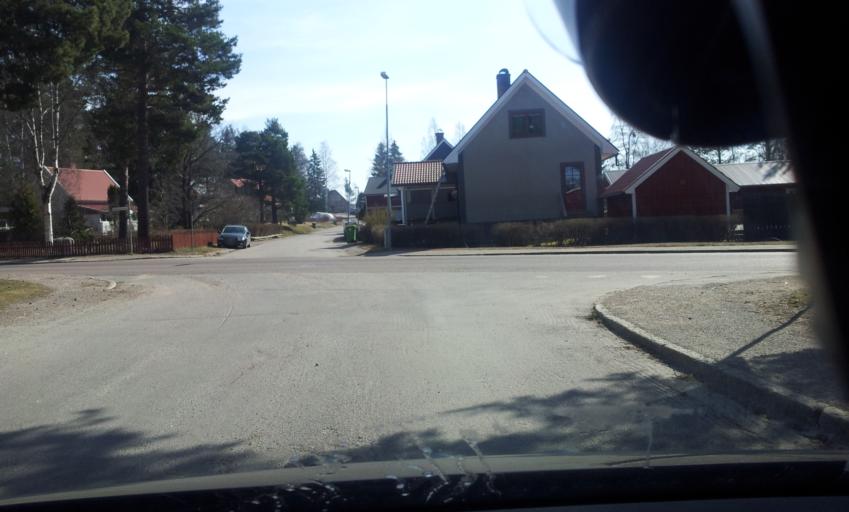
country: SE
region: Gaevleborg
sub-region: Ljusdals Kommun
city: Ljusdal
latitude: 61.8280
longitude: 16.1098
